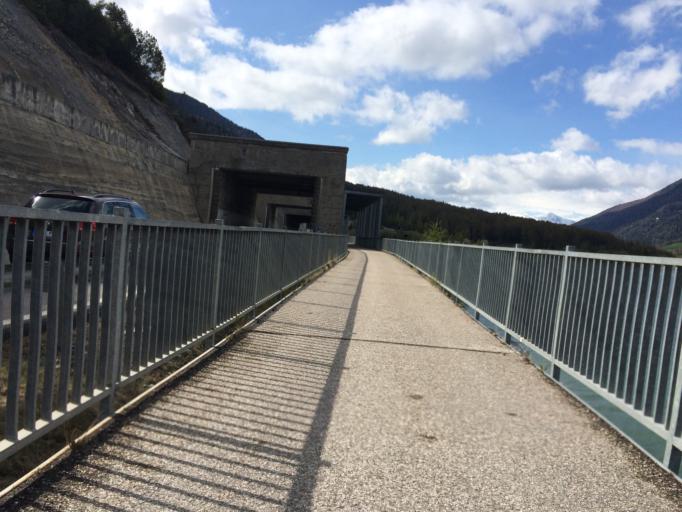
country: IT
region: Trentino-Alto Adige
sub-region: Bolzano
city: Curon Venosta
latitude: 46.7887
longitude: 10.5413
